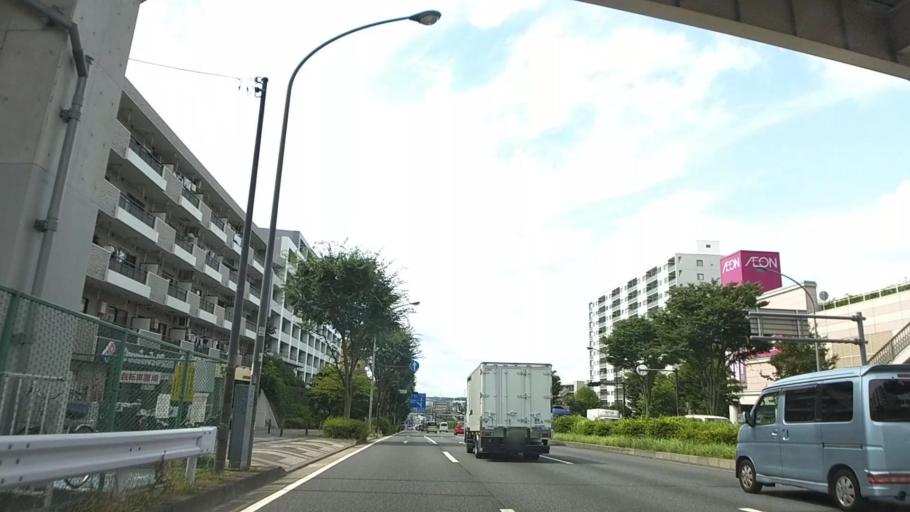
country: JP
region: Kanagawa
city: Yokohama
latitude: 35.4303
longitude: 139.5625
